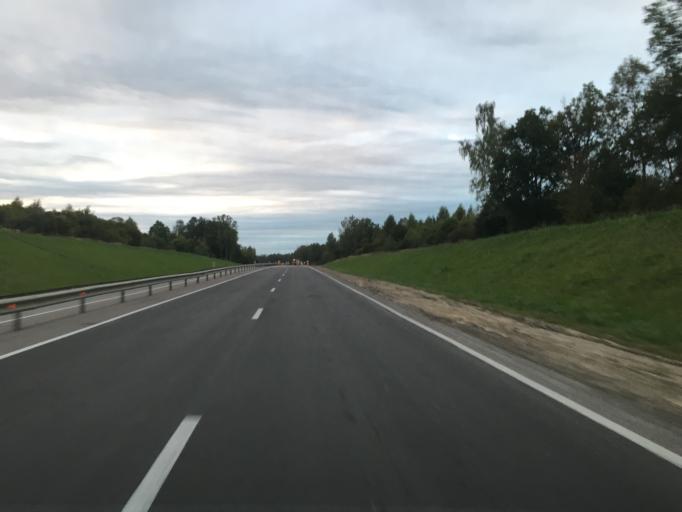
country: RU
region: Kaluga
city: Kaluga
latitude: 54.6046
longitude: 36.3154
